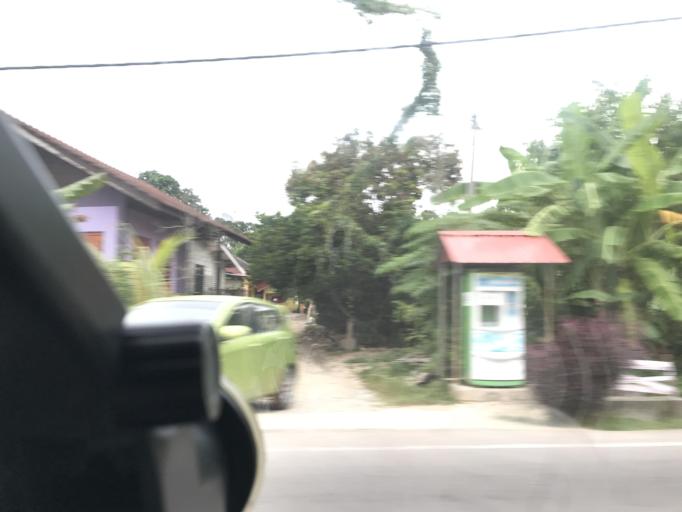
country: MY
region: Kelantan
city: Kota Bharu
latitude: 6.1267
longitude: 102.1749
